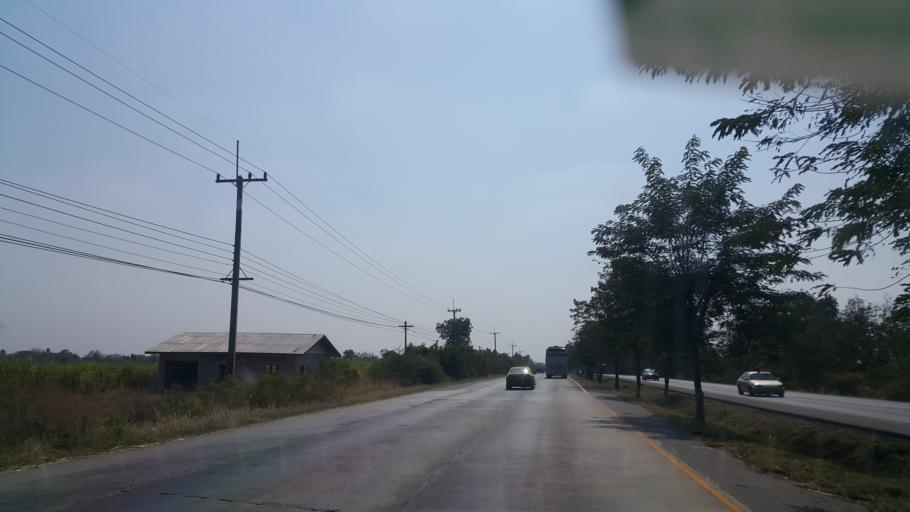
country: TH
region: Nakhon Ratchasima
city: Non Daeng
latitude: 15.3983
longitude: 102.4718
